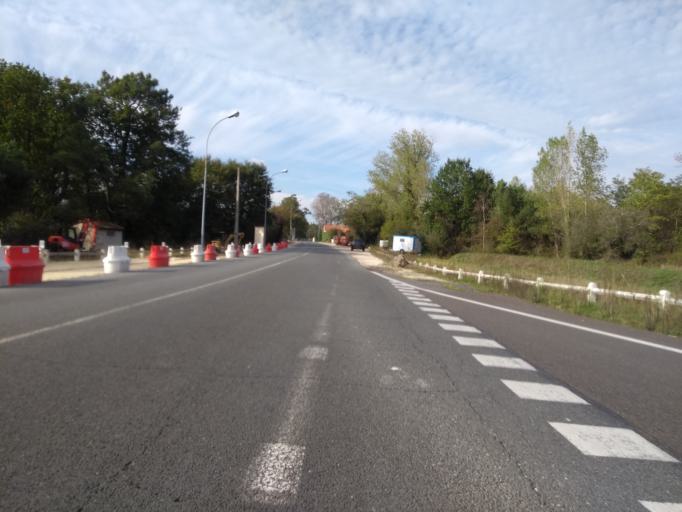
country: FR
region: Aquitaine
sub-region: Departement de la Gironde
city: Canejan
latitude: 44.7728
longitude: -0.6619
